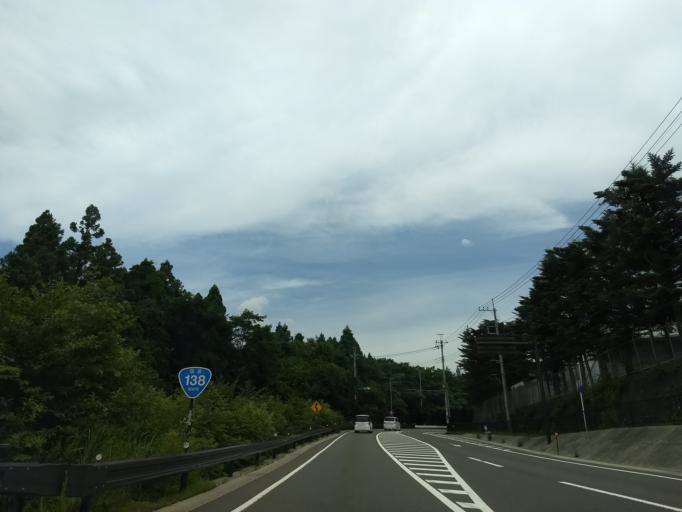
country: JP
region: Shizuoka
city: Gotemba
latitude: 35.3639
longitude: 138.8603
